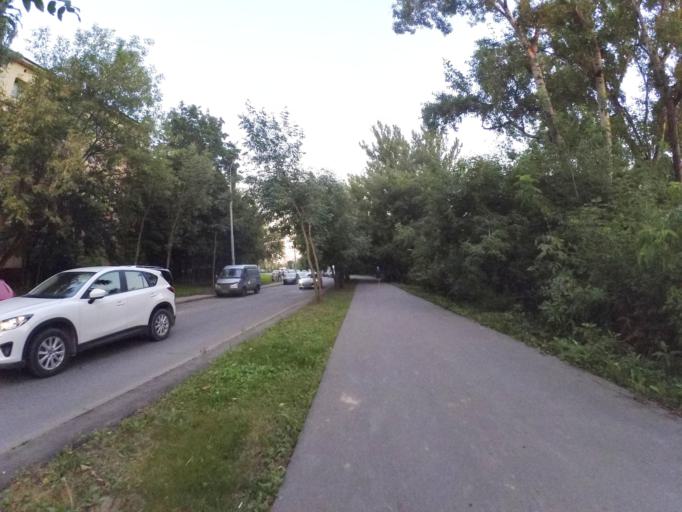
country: RU
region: Moscow
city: Strogino
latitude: 55.8433
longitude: 37.3999
